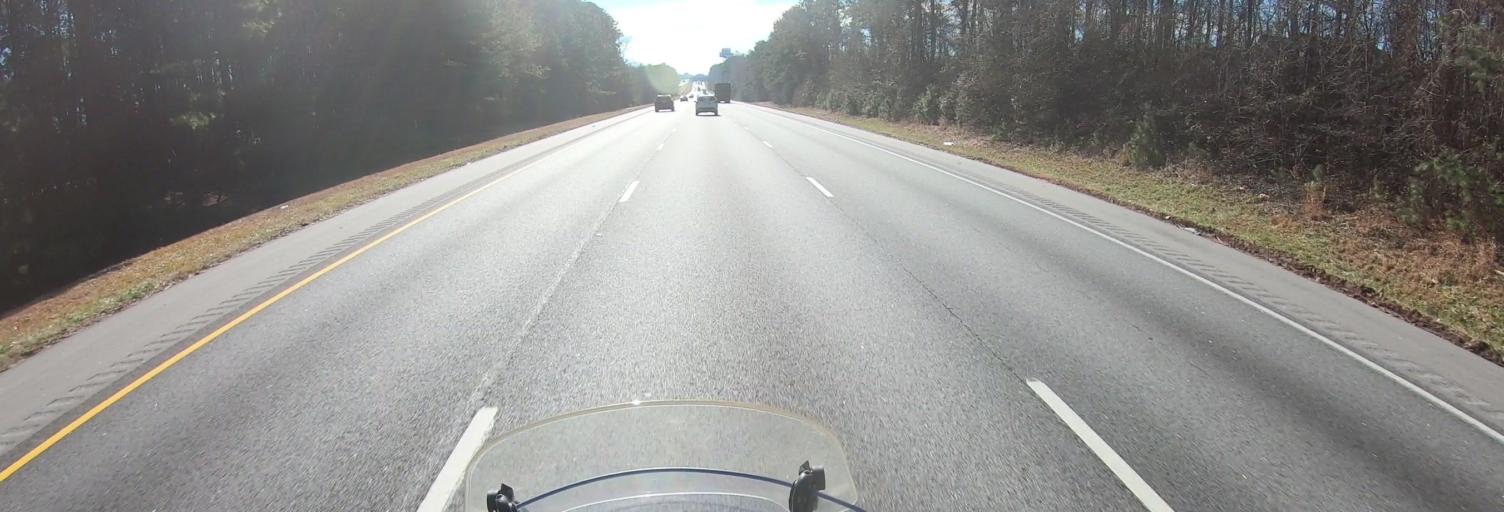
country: US
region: Georgia
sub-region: Henry County
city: Locust Grove
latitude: 33.3874
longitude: -84.1480
